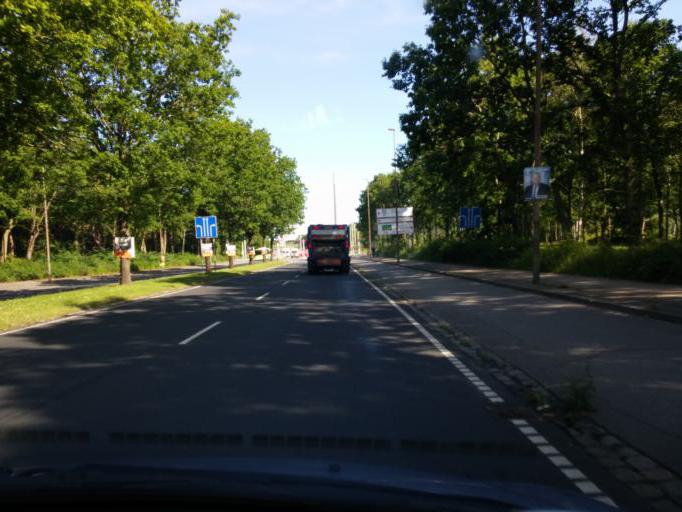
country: DK
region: South Denmark
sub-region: Odense Kommune
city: Seden
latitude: 55.4150
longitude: 10.4220
